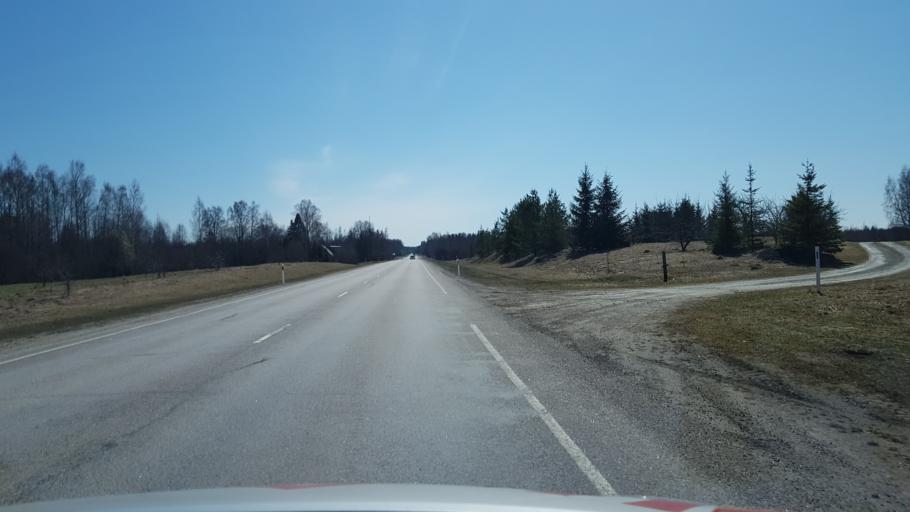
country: EE
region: Ida-Virumaa
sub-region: Johvi vald
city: Johvi
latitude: 59.1792
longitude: 27.3489
